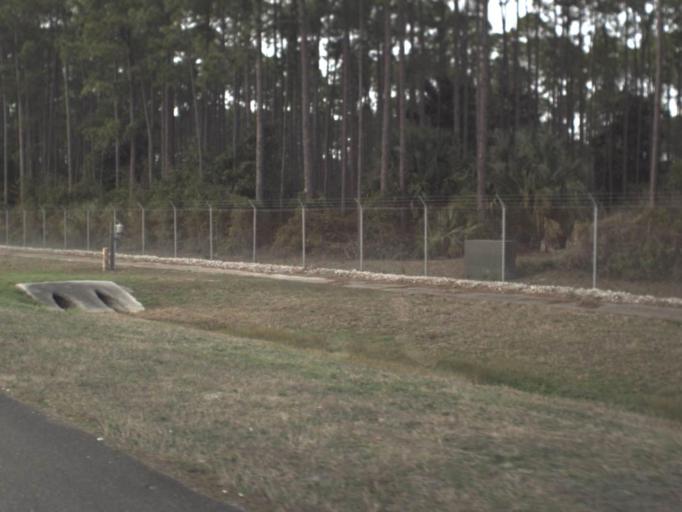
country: US
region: Florida
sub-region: Bay County
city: Tyndall Air Force Base
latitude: 30.0788
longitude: -85.6014
